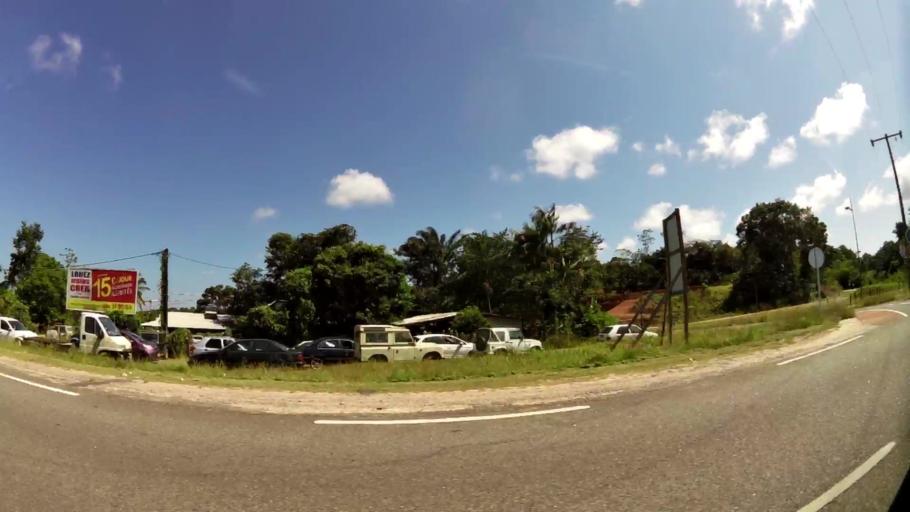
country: GF
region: Guyane
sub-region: Guyane
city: Matoury
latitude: 4.8366
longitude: -52.3445
